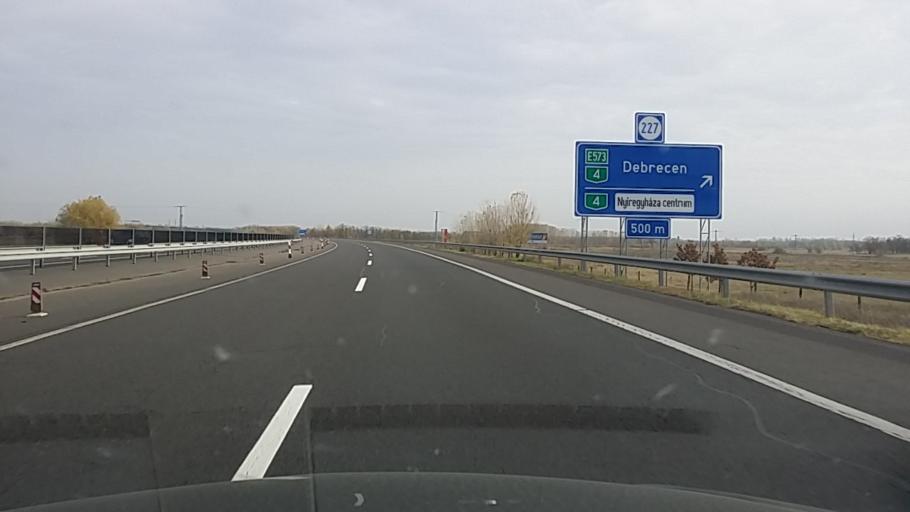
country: HU
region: Szabolcs-Szatmar-Bereg
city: Nyiregyhaza
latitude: 47.8863
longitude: 21.6988
